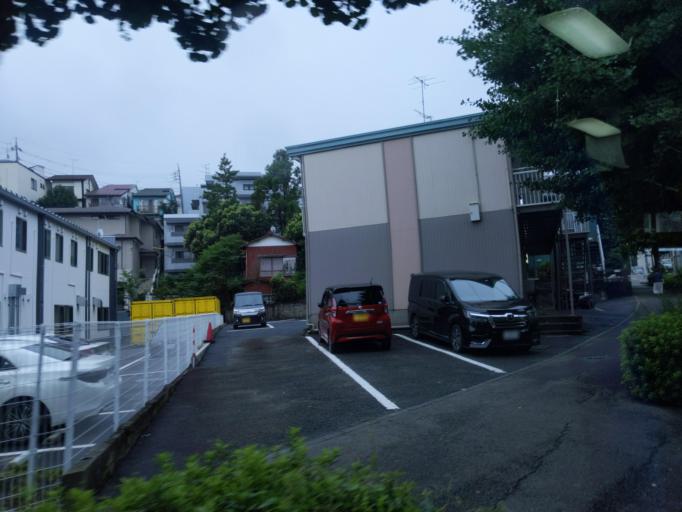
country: JP
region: Tokyo
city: Chofugaoka
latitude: 35.5925
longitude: 139.5679
